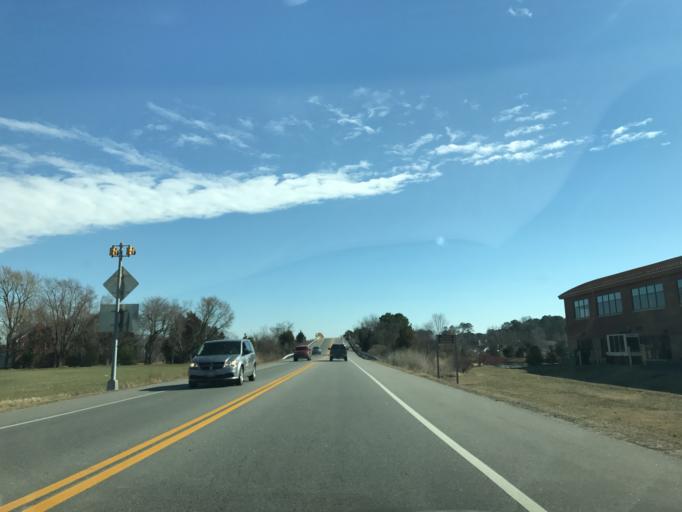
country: US
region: Maryland
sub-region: Queen Anne's County
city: Chester
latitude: 38.9777
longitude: -76.2865
